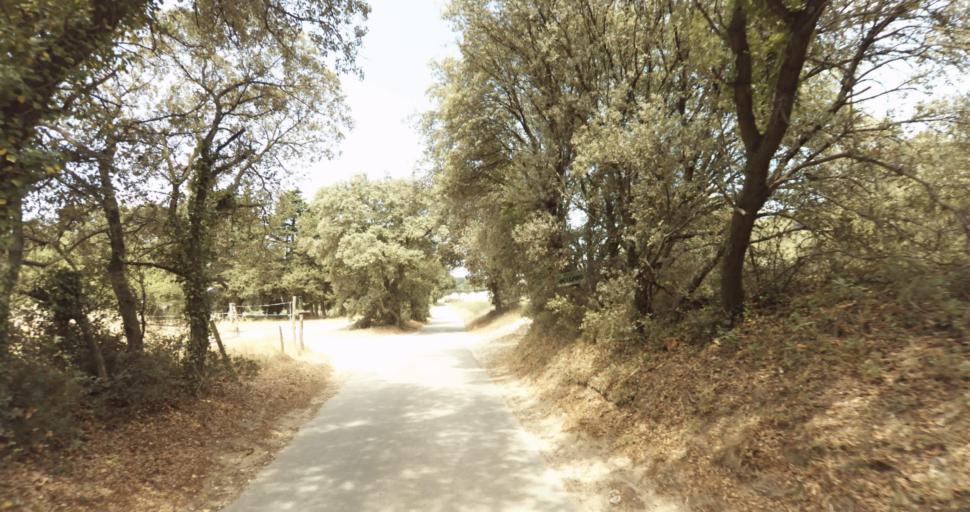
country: FR
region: Provence-Alpes-Cote d'Azur
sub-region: Departement du Vaucluse
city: Loriol-du-Comtat
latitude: 44.0594
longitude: 4.9930
